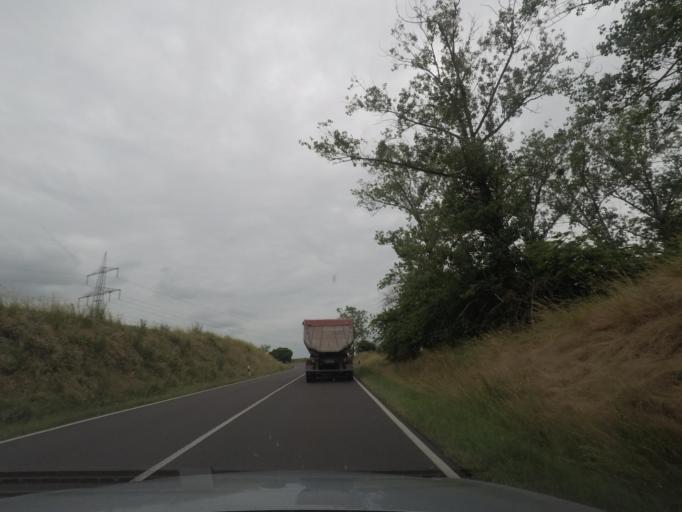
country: DE
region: Saxony-Anhalt
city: Suplingen
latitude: 52.2296
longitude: 11.3131
